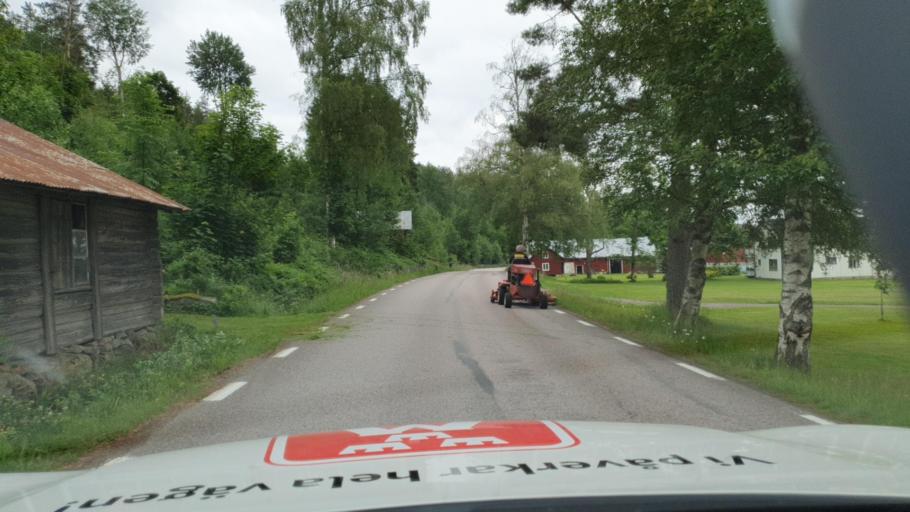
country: SE
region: Vaermland
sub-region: Kils Kommun
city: Kil
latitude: 59.6241
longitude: 13.3264
